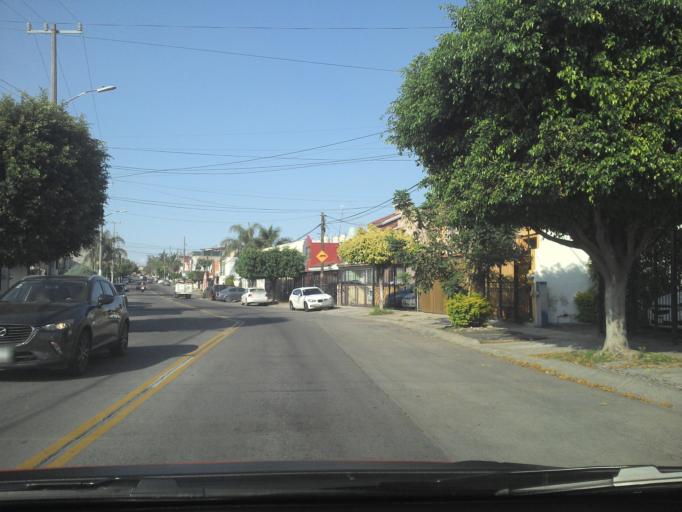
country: MX
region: Jalisco
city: Guadalajara
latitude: 20.6538
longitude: -103.4429
